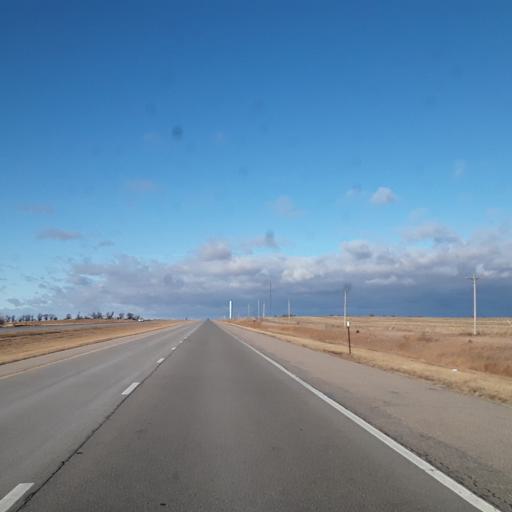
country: US
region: Kansas
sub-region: Republic County
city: Belleville
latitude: 39.8998
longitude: -97.6144
